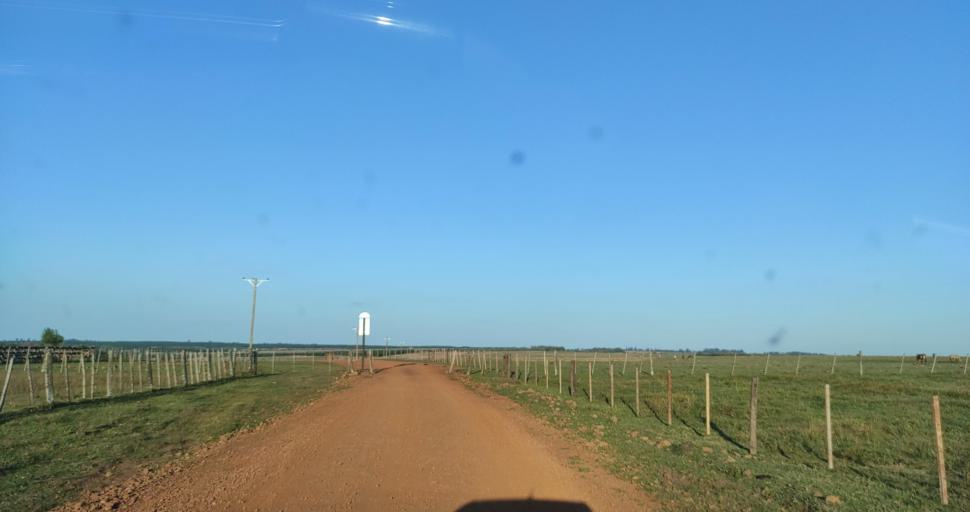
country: PY
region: Itapua
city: Carmen del Parana
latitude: -27.4106
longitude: -56.1527
